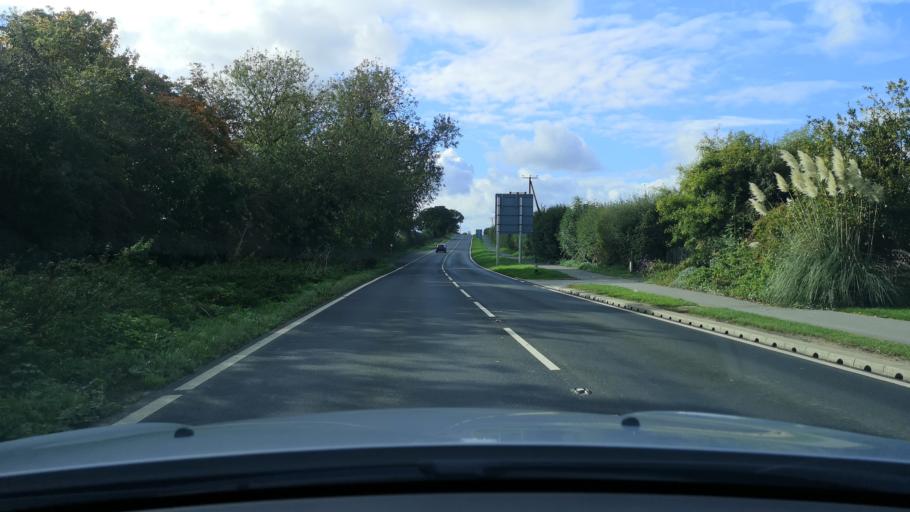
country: GB
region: England
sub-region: East Riding of Yorkshire
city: Leconfield
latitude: 53.8543
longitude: -0.4578
